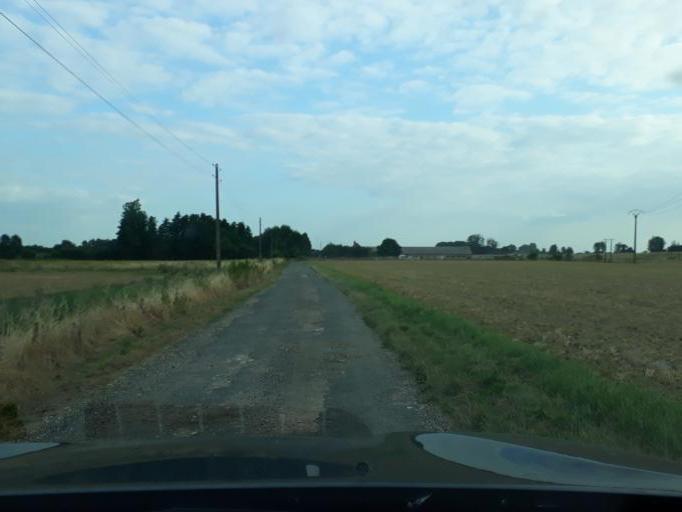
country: FR
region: Centre
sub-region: Departement du Loiret
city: Beaugency
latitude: 47.7655
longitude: 1.6385
